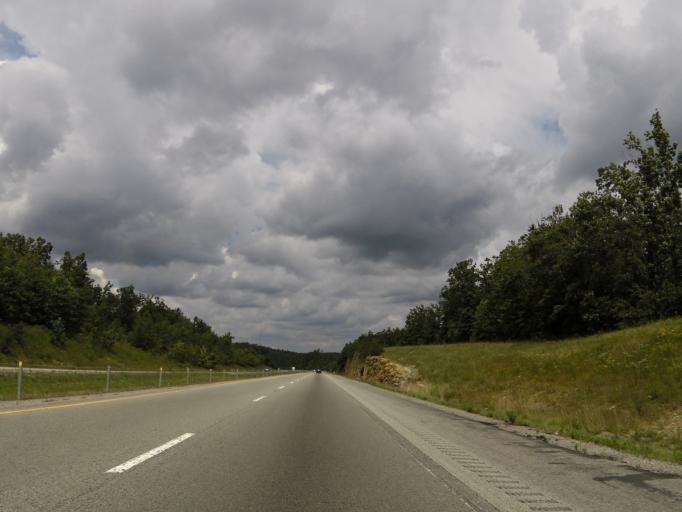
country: US
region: Tennessee
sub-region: Putnam County
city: Monterey
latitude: 36.1051
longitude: -85.2389
